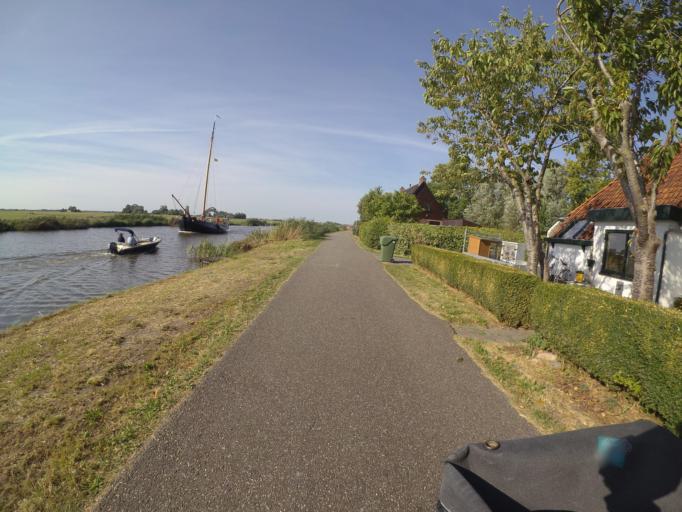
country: NL
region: Friesland
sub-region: Gemeente Dantumadiel
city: Rinsumageast
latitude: 53.3153
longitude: 5.9325
